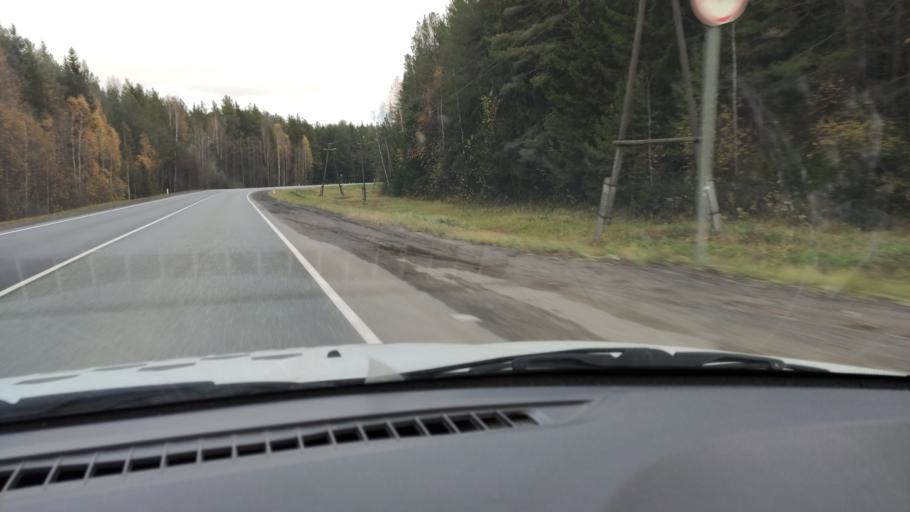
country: RU
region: Kirov
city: Belaya Kholunitsa
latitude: 58.8720
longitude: 50.8492
